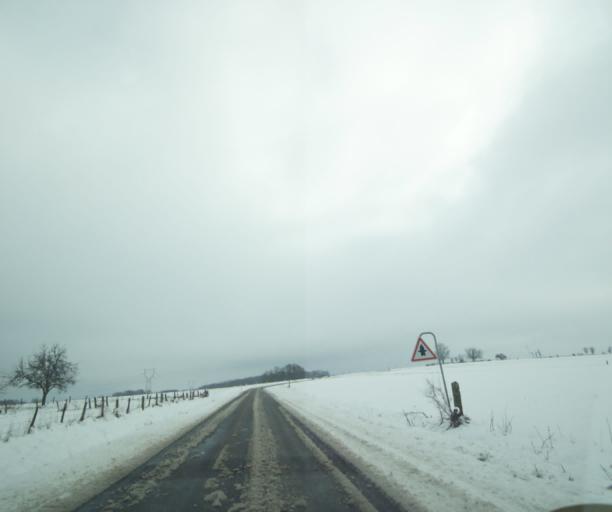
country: FR
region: Champagne-Ardenne
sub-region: Departement de la Haute-Marne
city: Montier-en-Der
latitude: 48.5072
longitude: 4.7297
